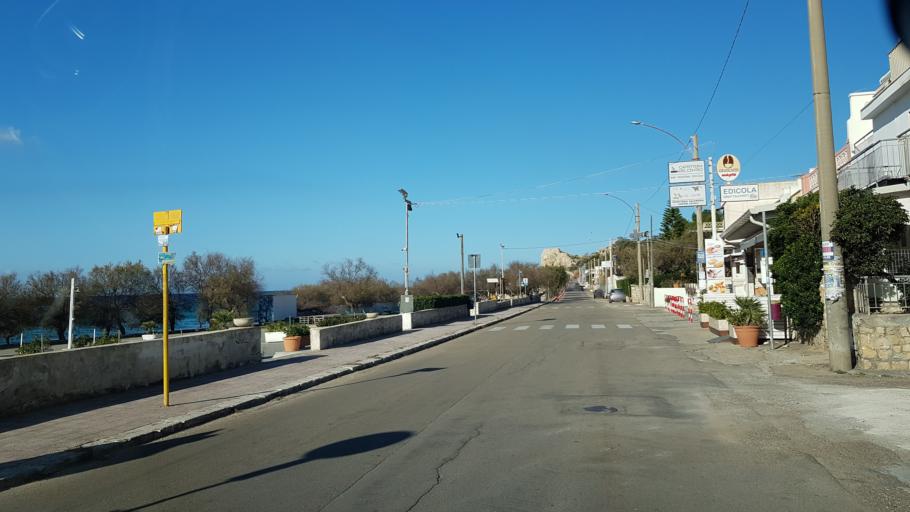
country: IT
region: Apulia
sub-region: Provincia di Lecce
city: Nardo
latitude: 40.1099
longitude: 18.0101
